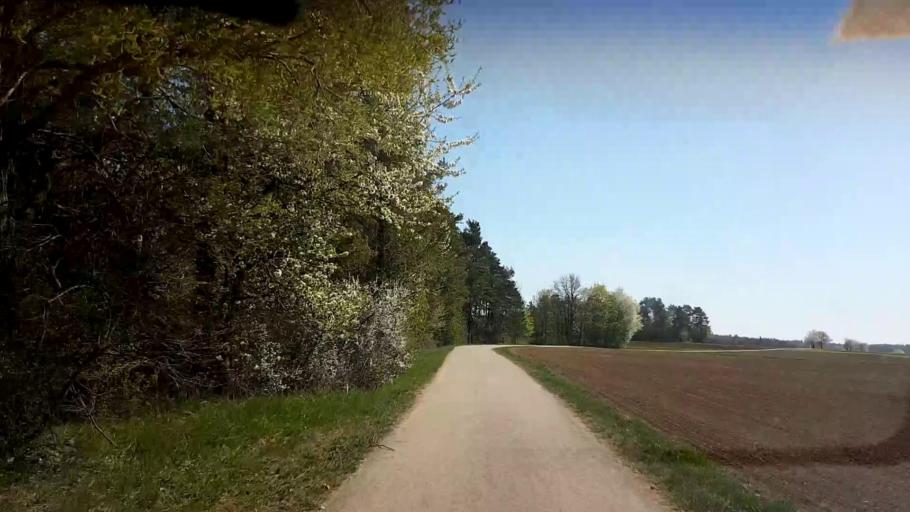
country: DE
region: Bavaria
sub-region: Upper Franconia
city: Konigsfeld
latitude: 49.9050
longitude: 11.1745
